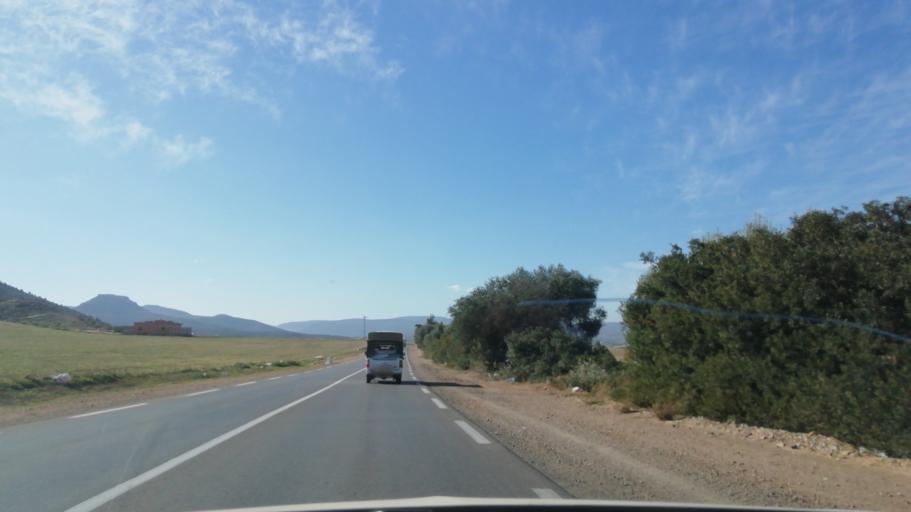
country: DZ
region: Tlemcen
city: Ouled Mimoun
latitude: 34.8833
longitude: -1.0851
